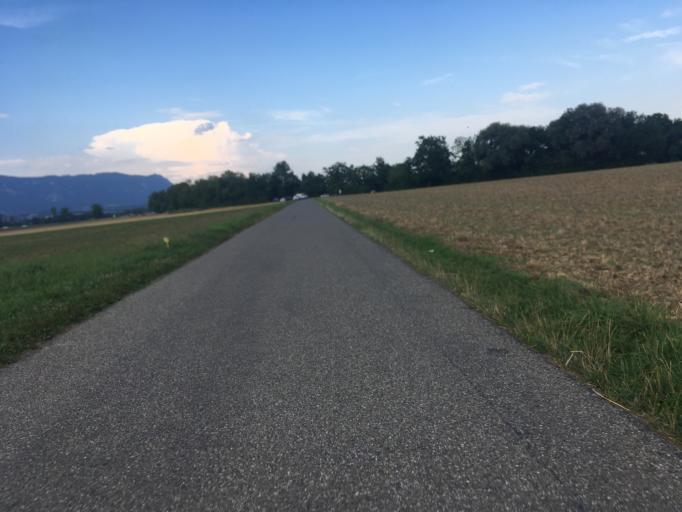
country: CH
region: Bern
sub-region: Seeland District
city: Arch
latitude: 47.1692
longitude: 7.4139
